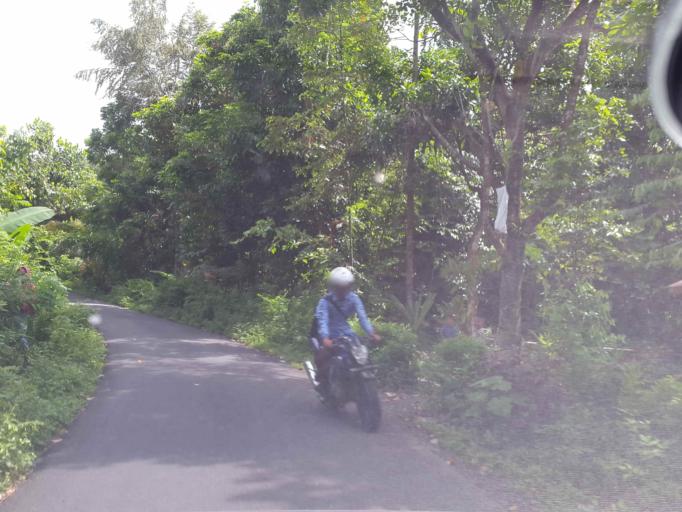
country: ID
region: West Nusa Tenggara
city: Dasangeria Selatan
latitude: -8.5454
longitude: 116.1492
